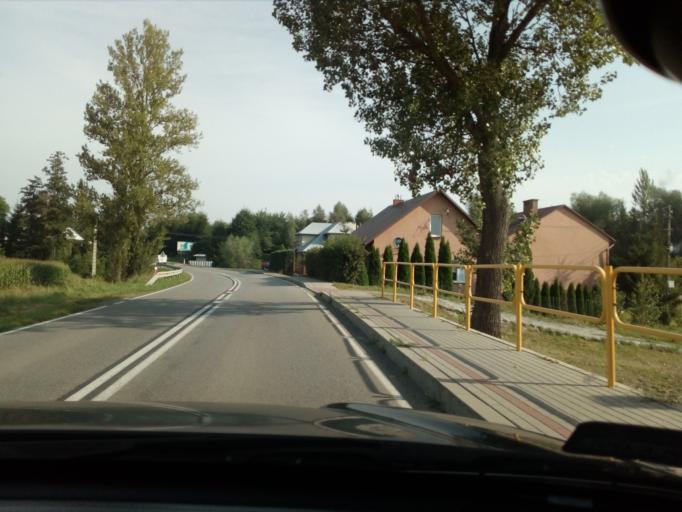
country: PL
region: Subcarpathian Voivodeship
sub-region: Powiat lancucki
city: Albigowa
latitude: 50.0394
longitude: 22.2304
